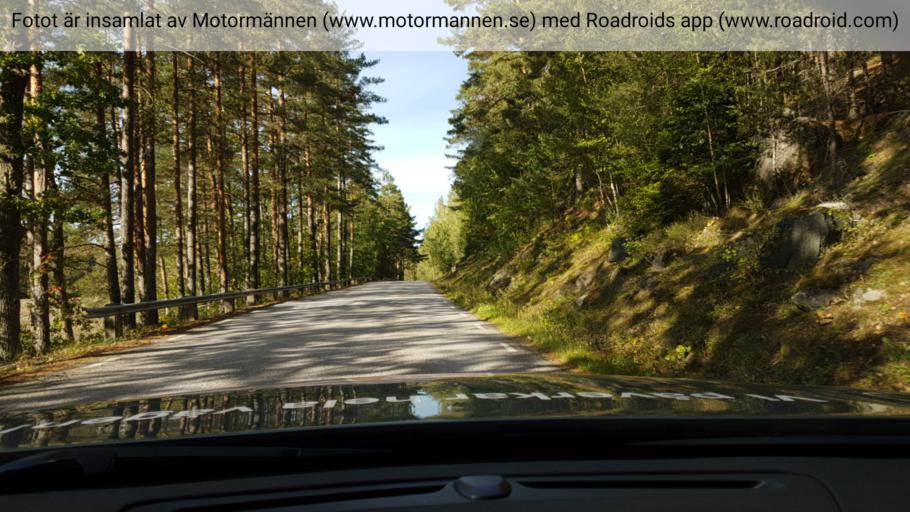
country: SE
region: OEstergoetland
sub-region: Valdemarsviks Kommun
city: Valdemarsvik
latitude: 58.1441
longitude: 16.6149
